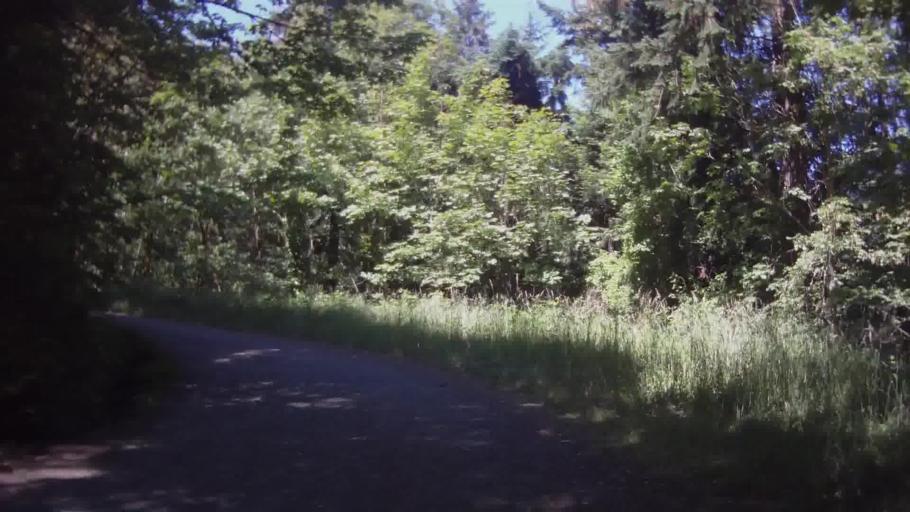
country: US
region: Oregon
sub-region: Washington County
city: West Haven-Sylvan
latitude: 45.5467
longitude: -122.7299
